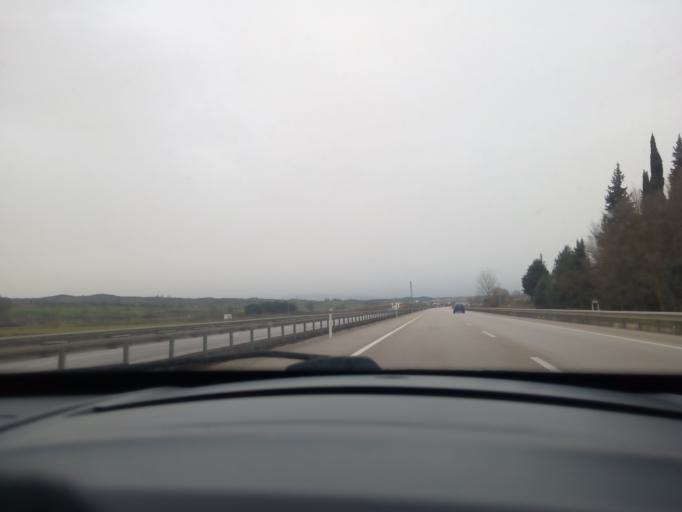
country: TR
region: Bursa
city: Tatkavakli
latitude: 40.0298
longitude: 28.3224
